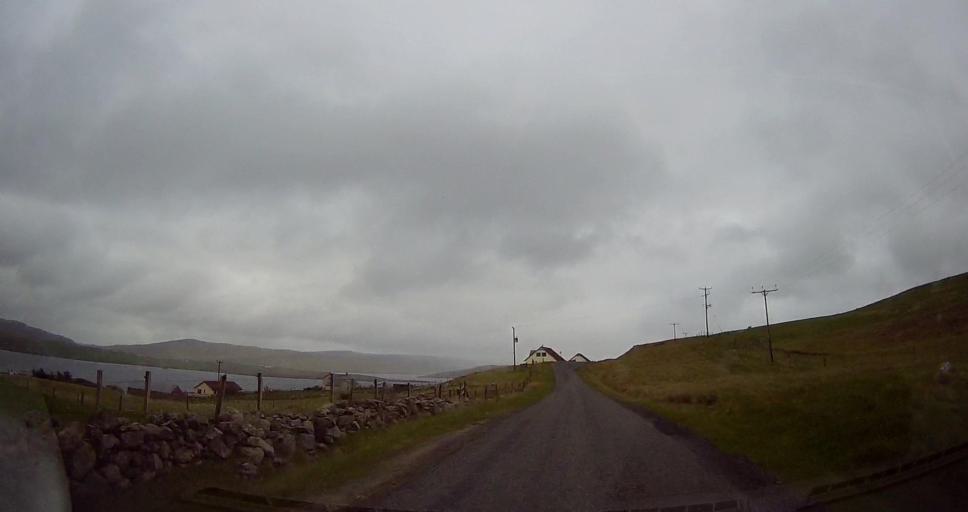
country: GB
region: Scotland
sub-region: Shetland Islands
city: Lerwick
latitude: 60.3846
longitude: -1.3799
